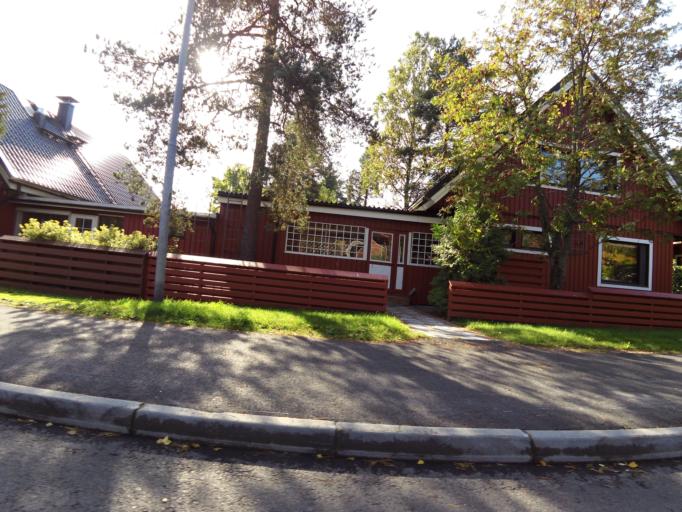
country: FI
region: Uusimaa
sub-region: Helsinki
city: Espoo
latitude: 60.1824
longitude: 24.6558
